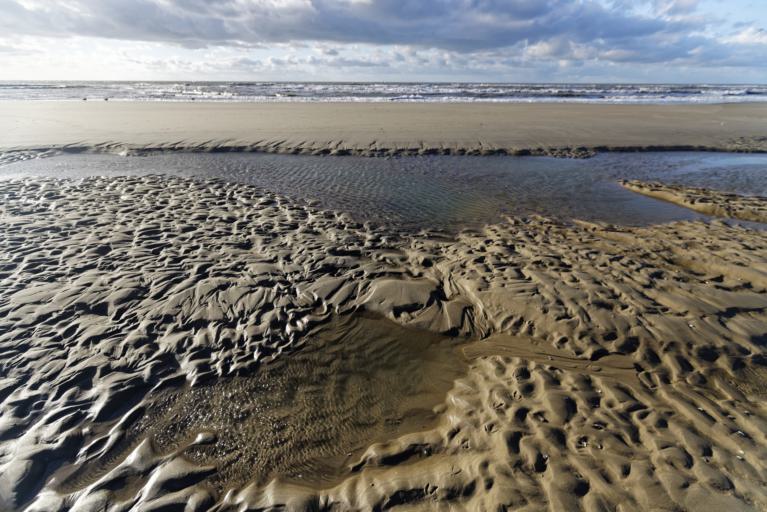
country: NL
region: North Holland
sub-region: Gemeente Den Helder
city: Den Helder
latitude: 53.0162
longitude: 4.7101
